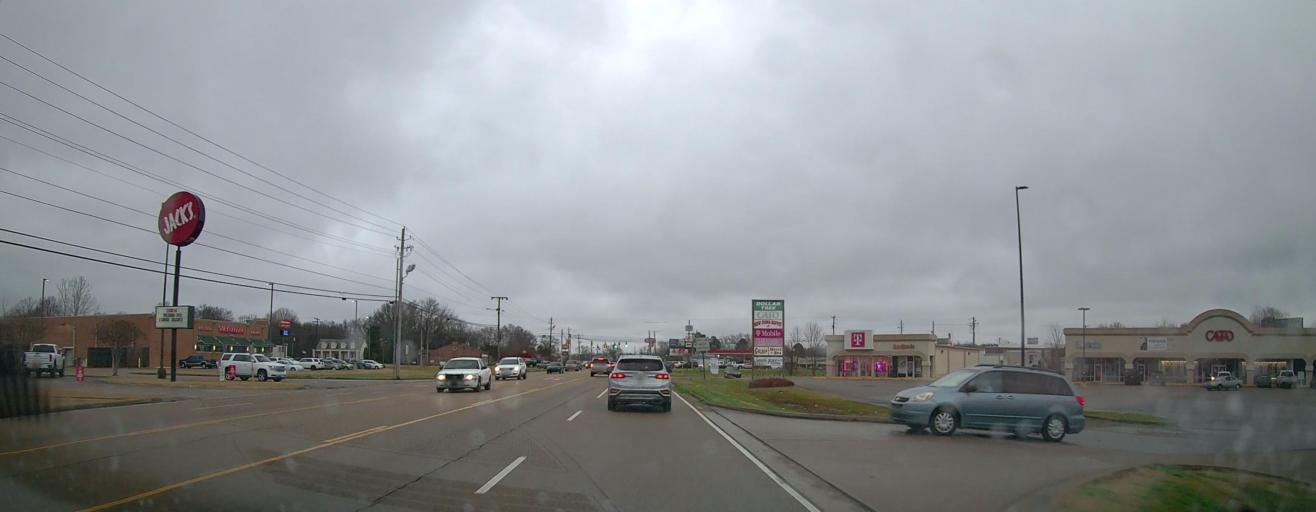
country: US
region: Mississippi
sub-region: Alcorn County
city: Corinth
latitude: 34.9127
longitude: -88.5022
